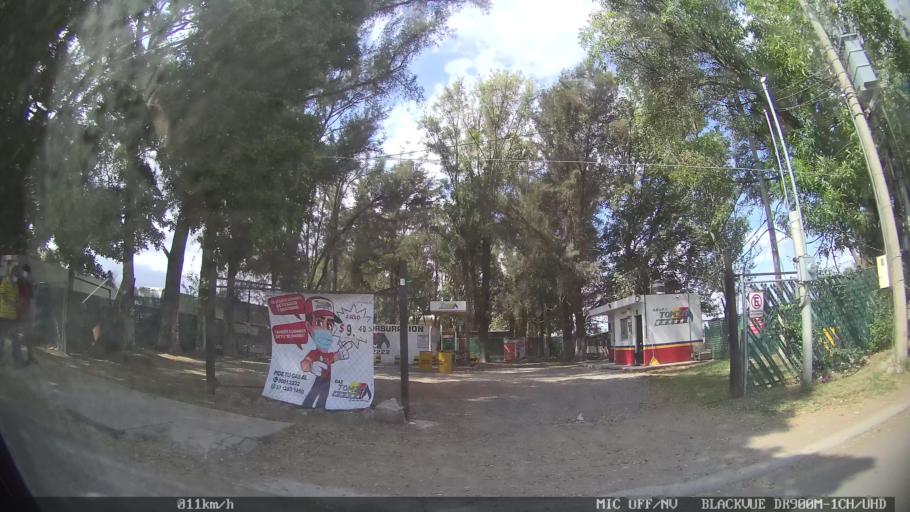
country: MX
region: Jalisco
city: Tonala
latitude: 20.6589
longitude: -103.2453
